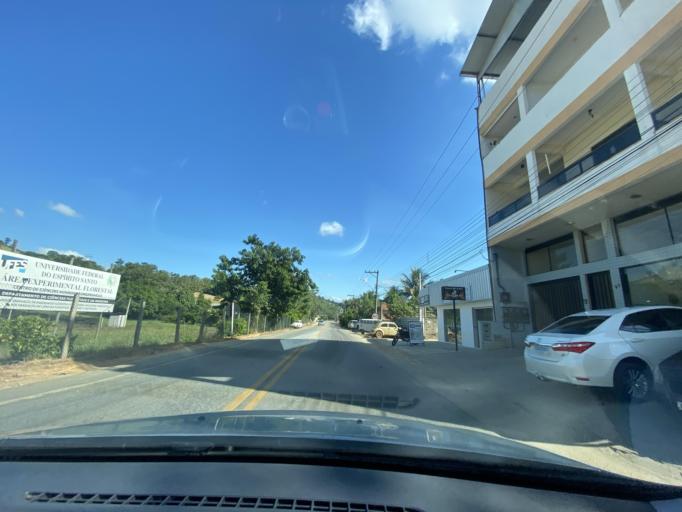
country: BR
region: Espirito Santo
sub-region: Jeronimo Monteiro
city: Jeronimo Monteiro
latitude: -20.7954
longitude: -41.4050
